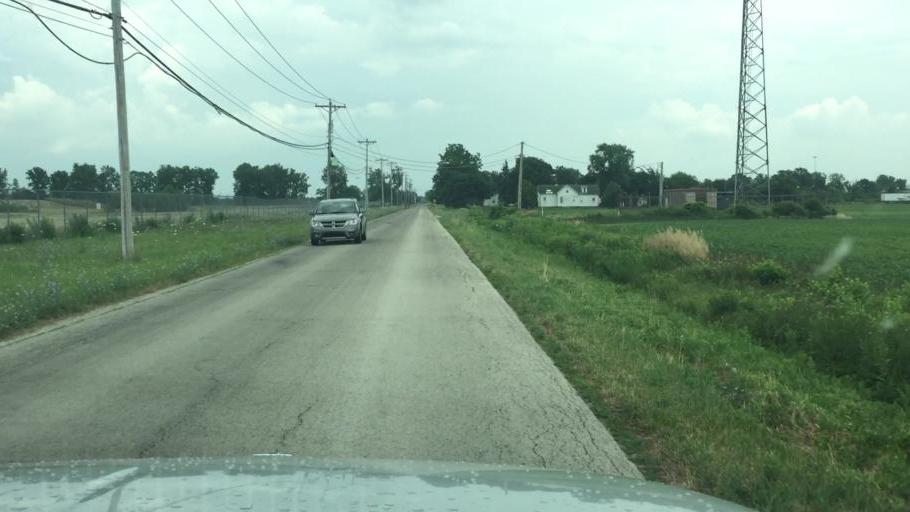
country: US
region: Ohio
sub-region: Wood County
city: Walbridge
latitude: 41.5879
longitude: -83.5233
